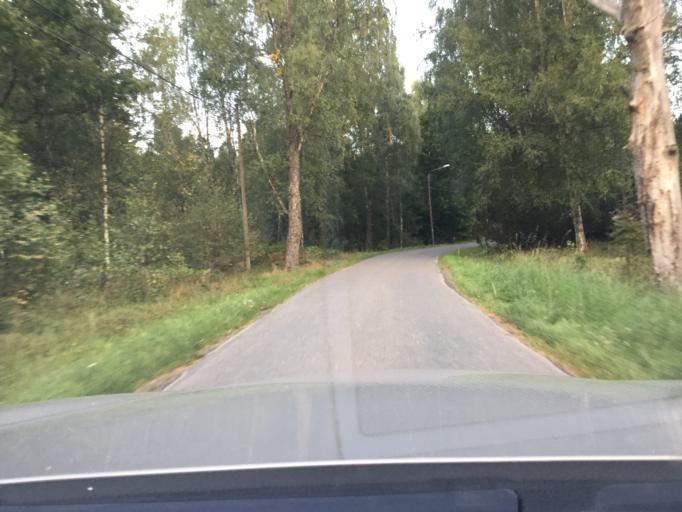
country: SE
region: Kronoberg
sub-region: Almhults Kommun
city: AElmhult
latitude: 56.6164
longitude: 14.2175
